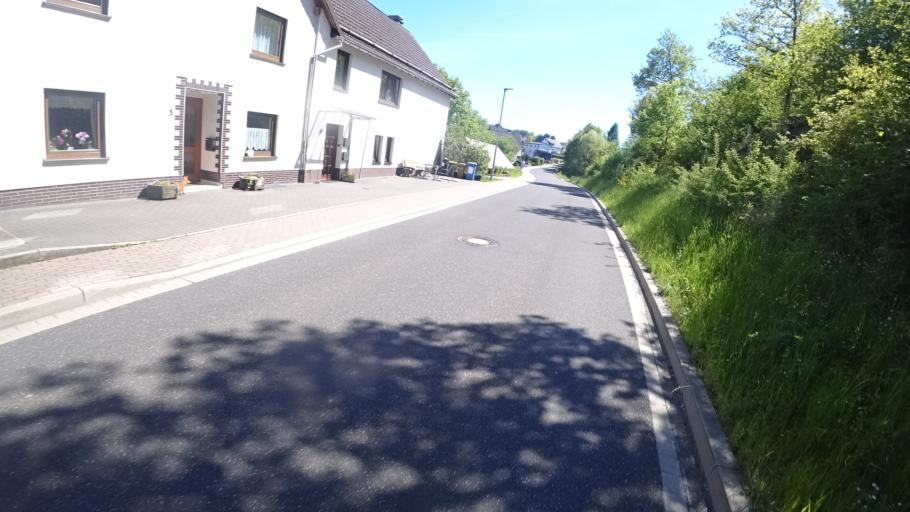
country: DE
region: Rheinland-Pfalz
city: Steineroth
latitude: 50.7439
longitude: 7.8536
